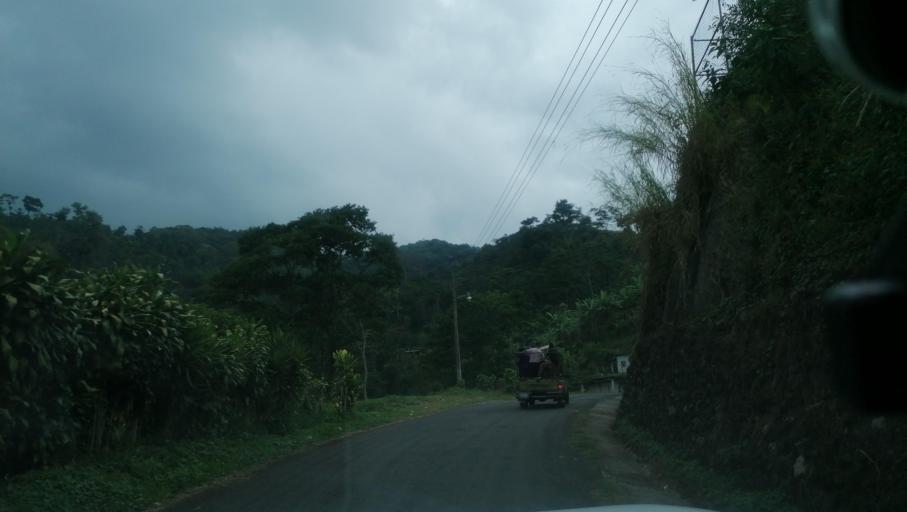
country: MX
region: Chiapas
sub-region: Cacahoatan
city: Benito Juarez
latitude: 15.0749
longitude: -92.1720
